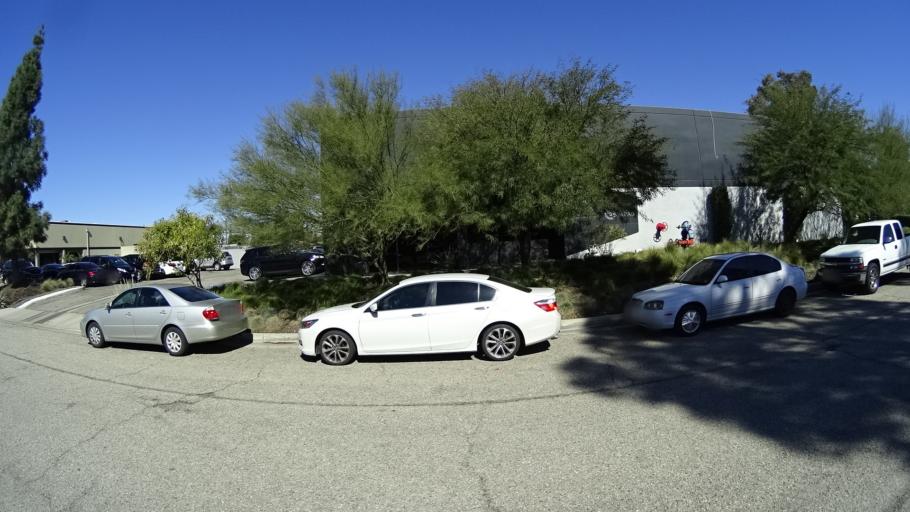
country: US
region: California
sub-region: Orange County
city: Yorba Linda
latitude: 33.8656
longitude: -117.8225
